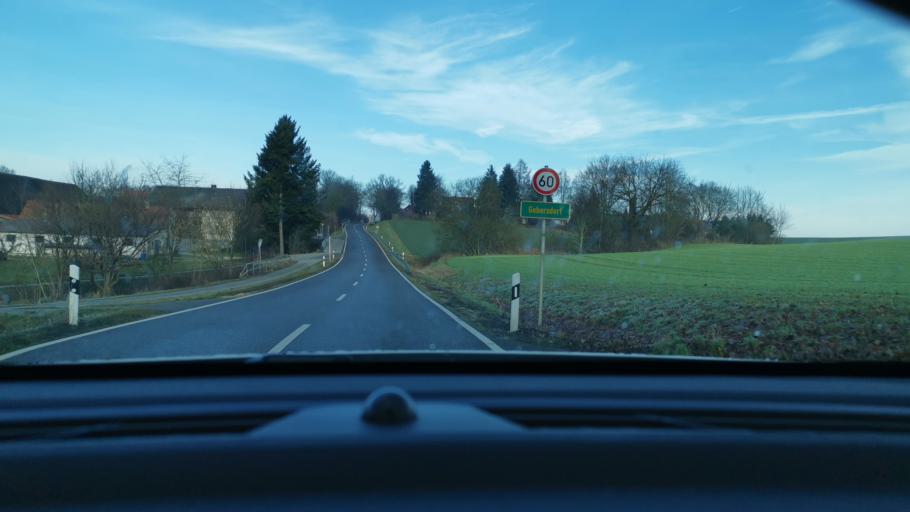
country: DE
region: Bavaria
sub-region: Swabia
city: Petersdorf
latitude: 48.5160
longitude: 11.0350
